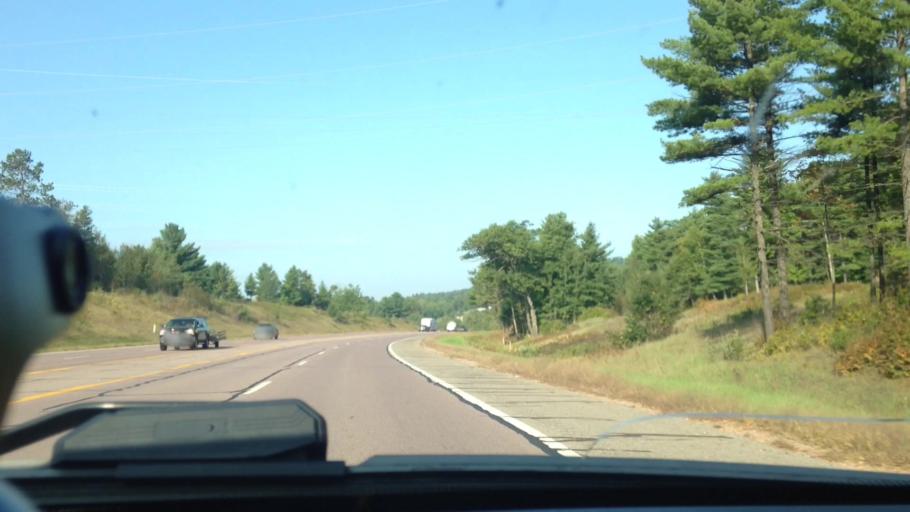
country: US
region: Michigan
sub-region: Dickinson County
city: Quinnesec
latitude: 45.8044
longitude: -87.9717
